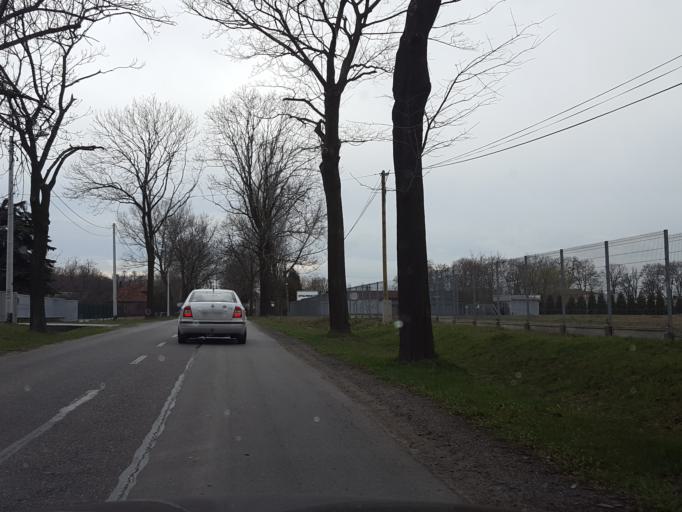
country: PL
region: Silesian Voivodeship
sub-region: Powiat gliwicki
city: Paniowki
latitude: 50.2111
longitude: 18.8170
